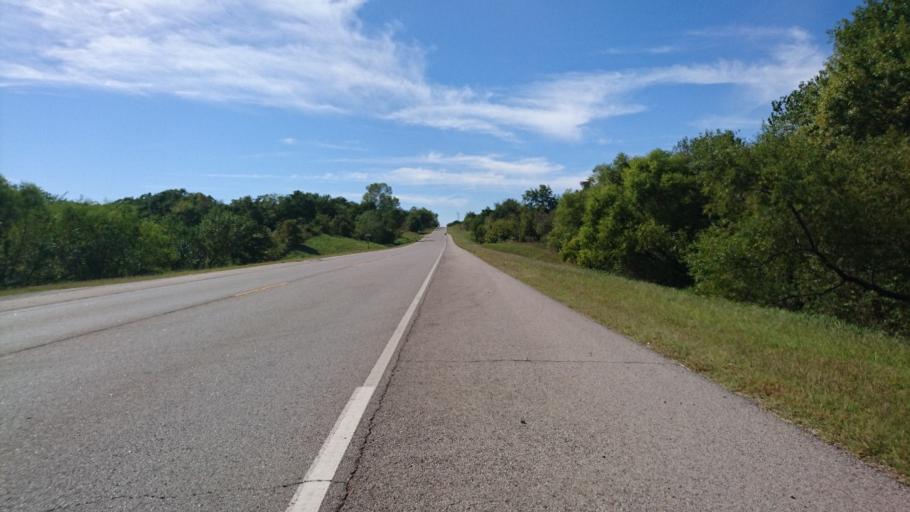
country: US
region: Oklahoma
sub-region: Lincoln County
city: Stroud
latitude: 35.7241
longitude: -96.7466
